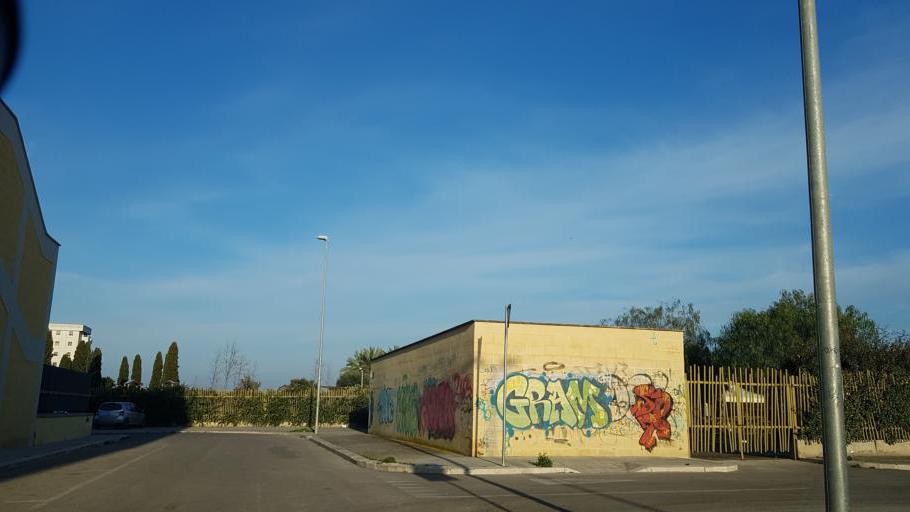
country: IT
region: Apulia
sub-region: Provincia di Brindisi
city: Brindisi
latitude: 40.6261
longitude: 17.9365
